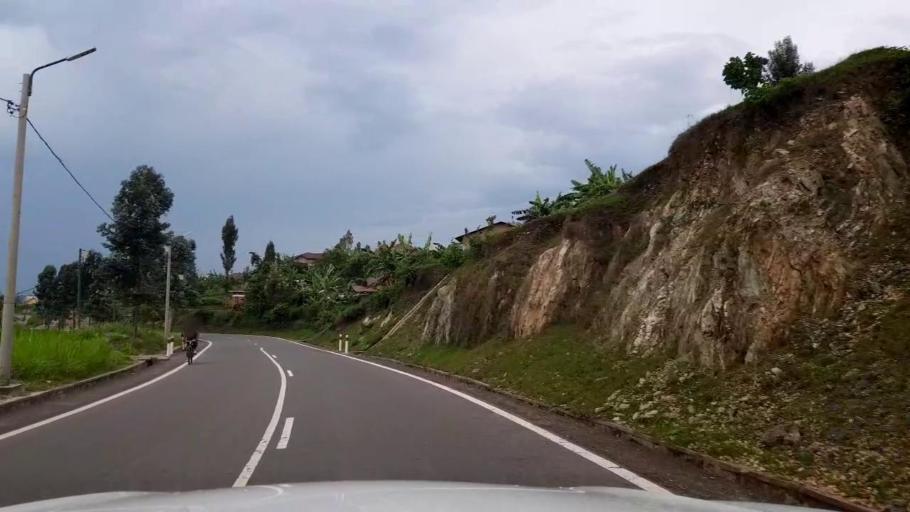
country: RW
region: Western Province
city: Kibuye
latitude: -2.0441
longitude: 29.4082
